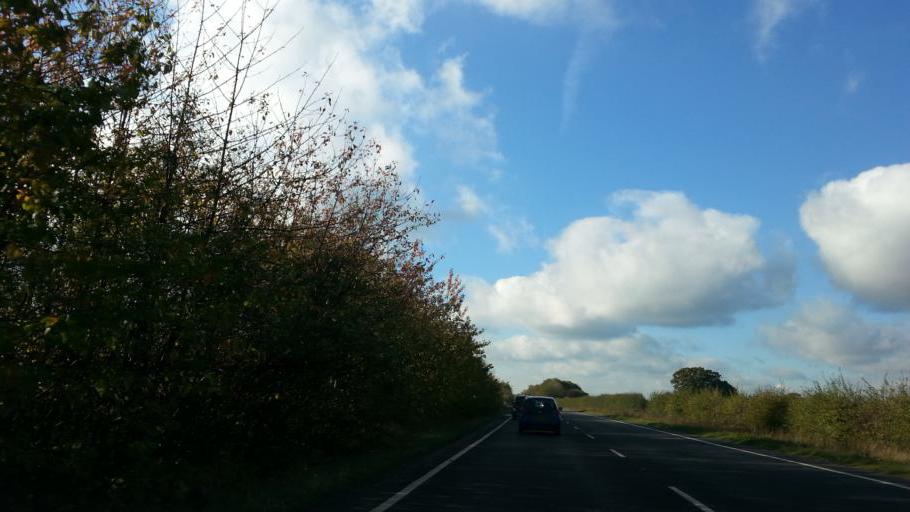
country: GB
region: England
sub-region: Norfolk
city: Loddon
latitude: 52.4845
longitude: 1.5127
